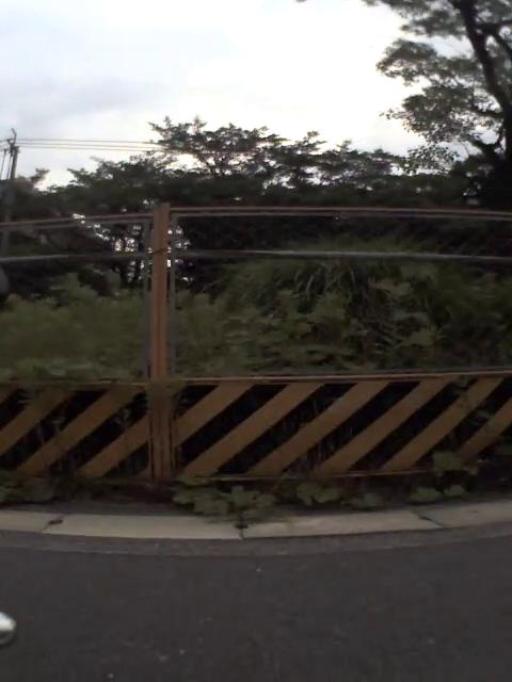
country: JP
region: Osaka
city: Hirakata
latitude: 34.7971
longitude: 135.6469
